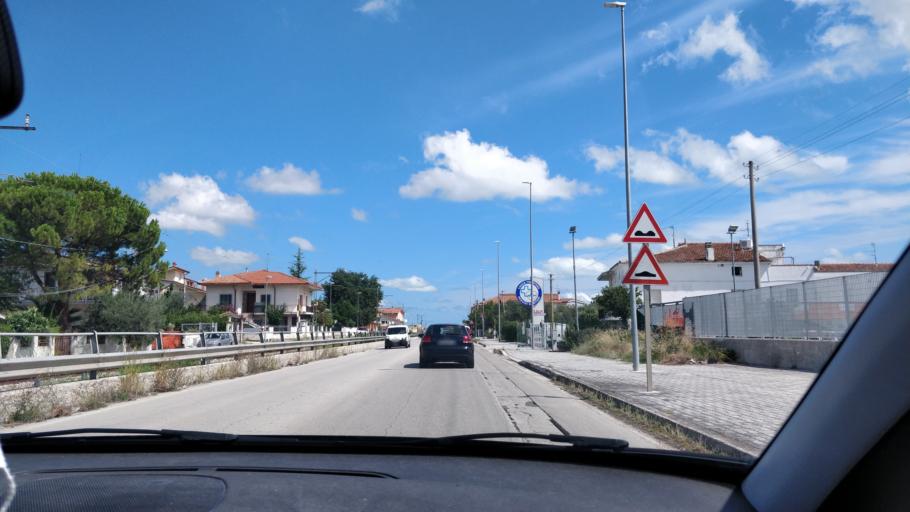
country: IT
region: Abruzzo
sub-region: Provincia di Chieti
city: Treglio
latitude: 42.2563
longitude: 14.4289
